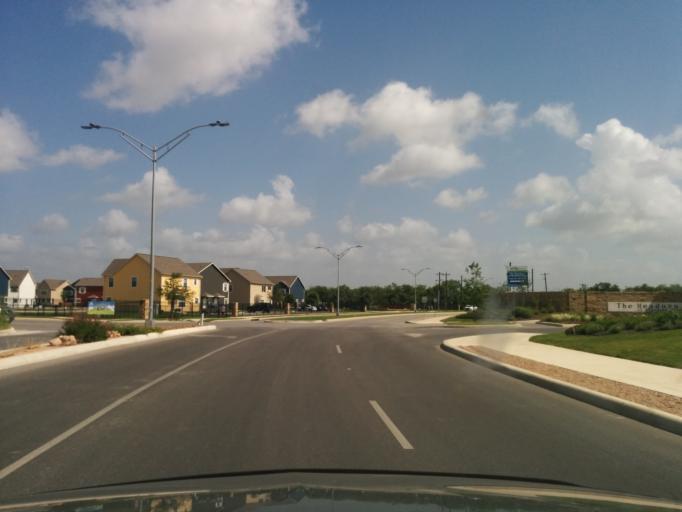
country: US
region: Texas
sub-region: Bexar County
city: Shavano Park
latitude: 29.5664
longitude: -98.6176
